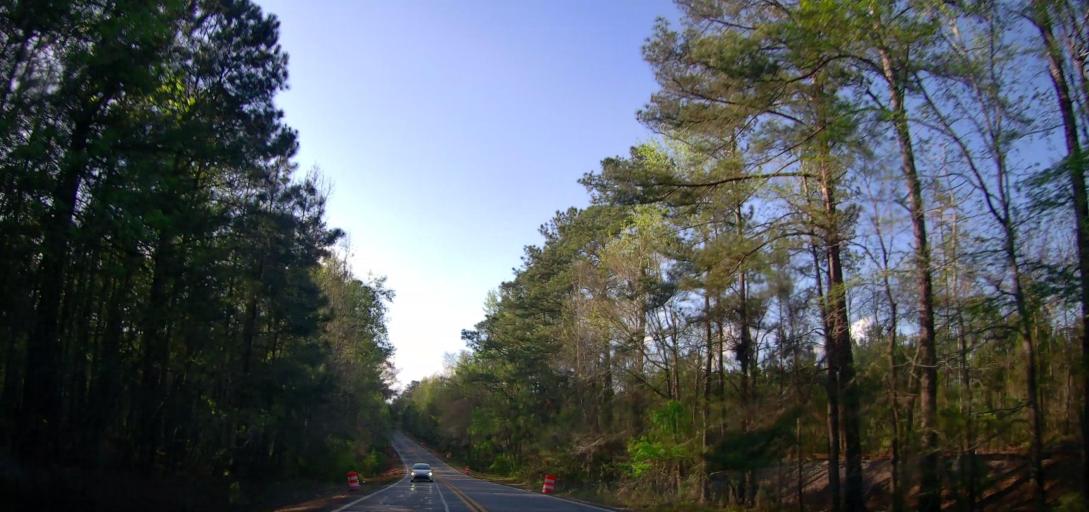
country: US
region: Georgia
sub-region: Baldwin County
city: Milledgeville
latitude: 33.1209
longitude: -83.2918
